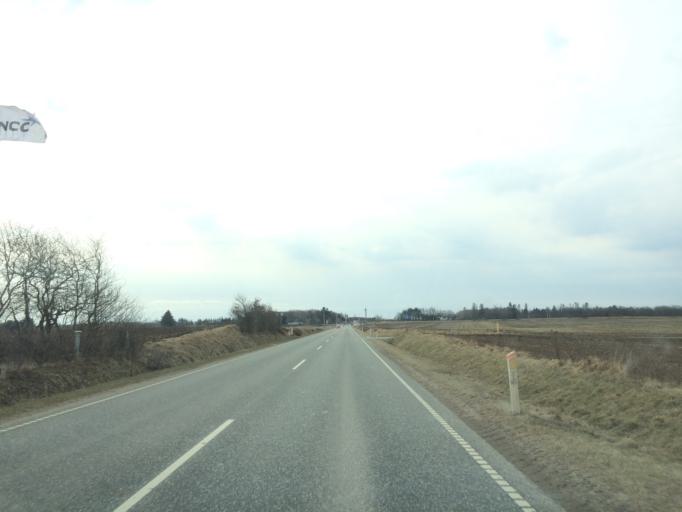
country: DK
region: Central Jutland
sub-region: Ringkobing-Skjern Kommune
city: Videbaek
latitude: 56.0915
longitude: 8.5075
